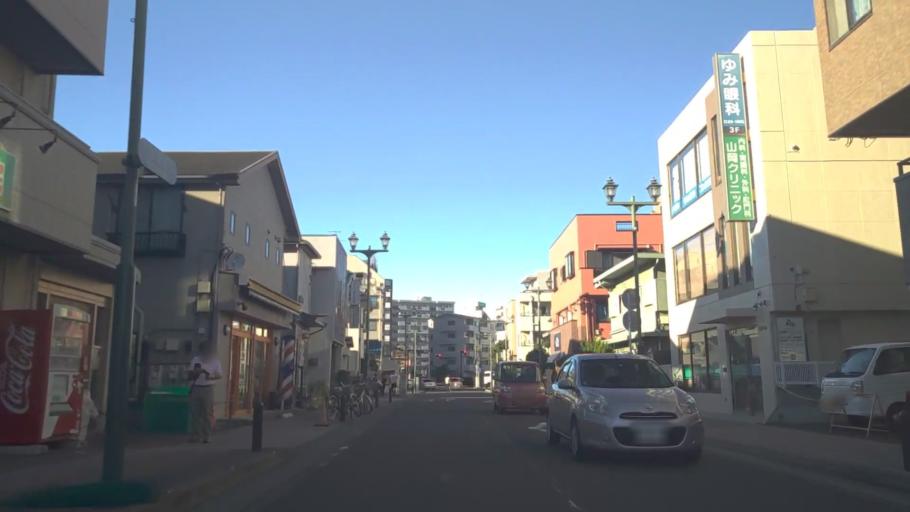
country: JP
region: Kanagawa
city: Chigasaki
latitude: 35.3322
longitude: 139.4069
